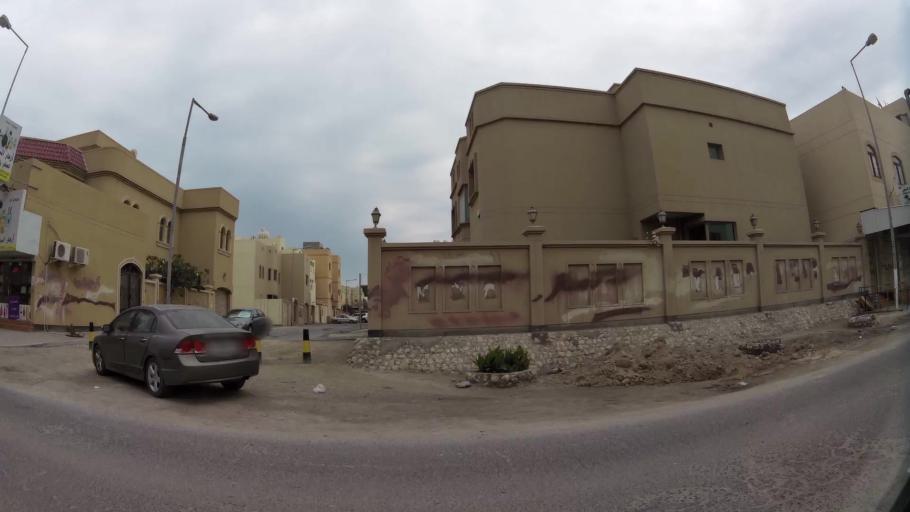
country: BH
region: Northern
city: Sitrah
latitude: 26.1674
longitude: 50.6124
